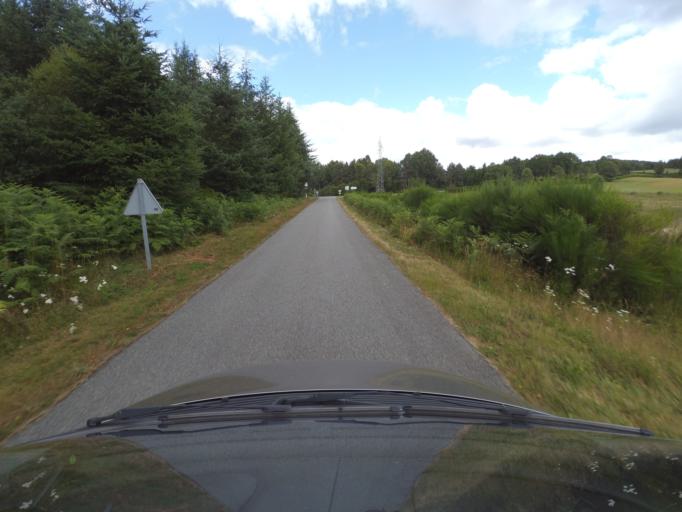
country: FR
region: Limousin
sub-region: Departement de la Creuse
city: Banize
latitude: 45.7579
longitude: 1.9538
